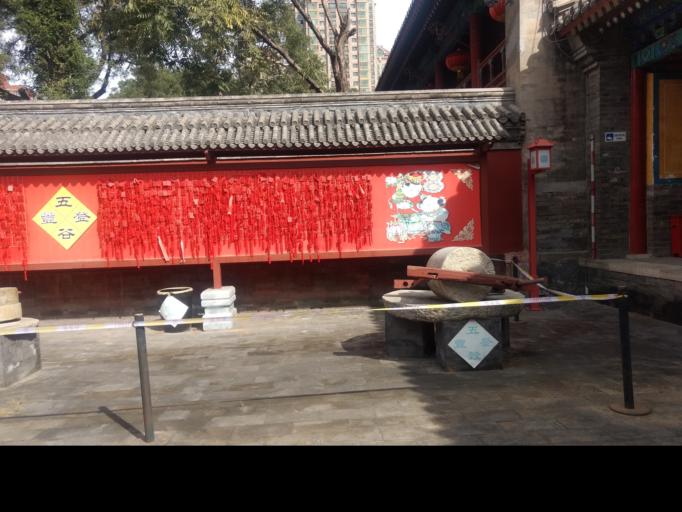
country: CN
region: Beijing
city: Chaowai
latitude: 39.9241
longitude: 116.4381
